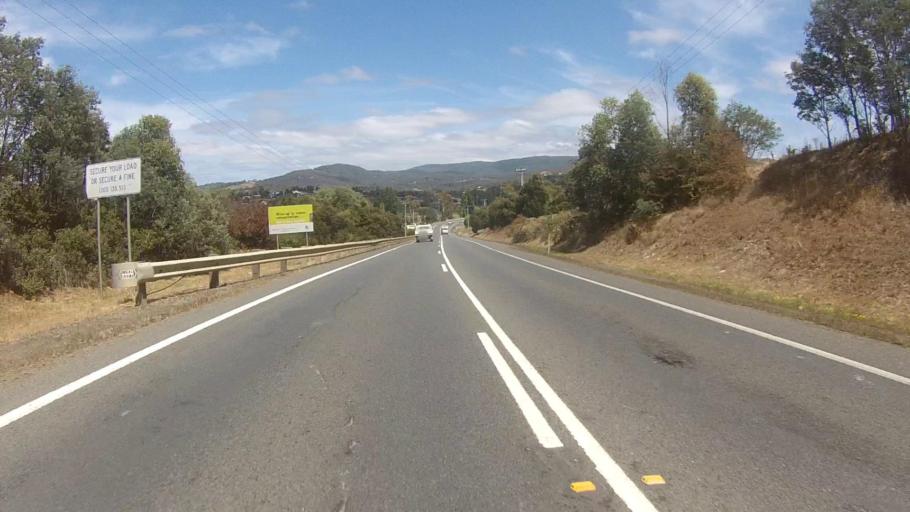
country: AU
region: Tasmania
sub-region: Kingborough
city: Margate
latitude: -43.0190
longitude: 147.2692
